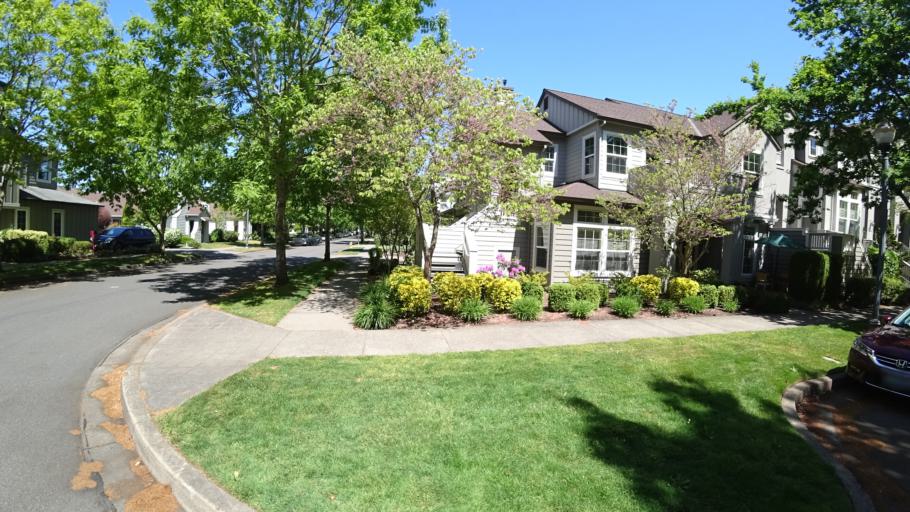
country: US
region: Oregon
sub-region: Washington County
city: Rockcreek
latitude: 45.5353
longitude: -122.9134
